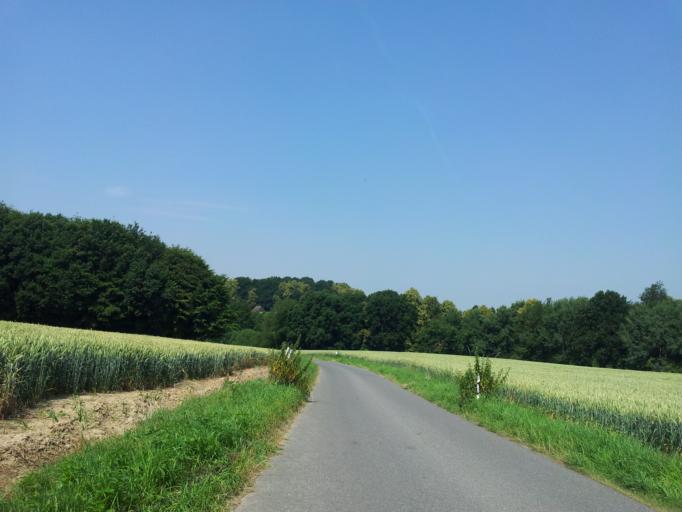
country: DE
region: Saxony
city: Panschwitz-Kuckau
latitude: 51.2129
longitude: 14.2056
